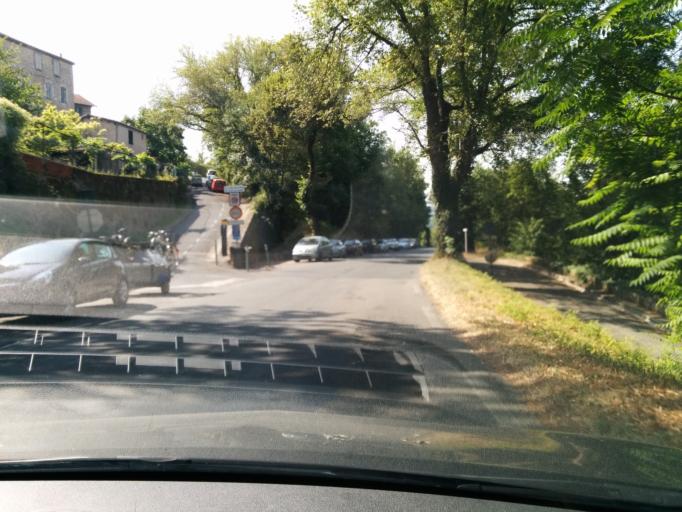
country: FR
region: Midi-Pyrenees
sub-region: Departement du Tarn
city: Cordes-sur-Ciel
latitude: 44.0650
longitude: 1.9540
